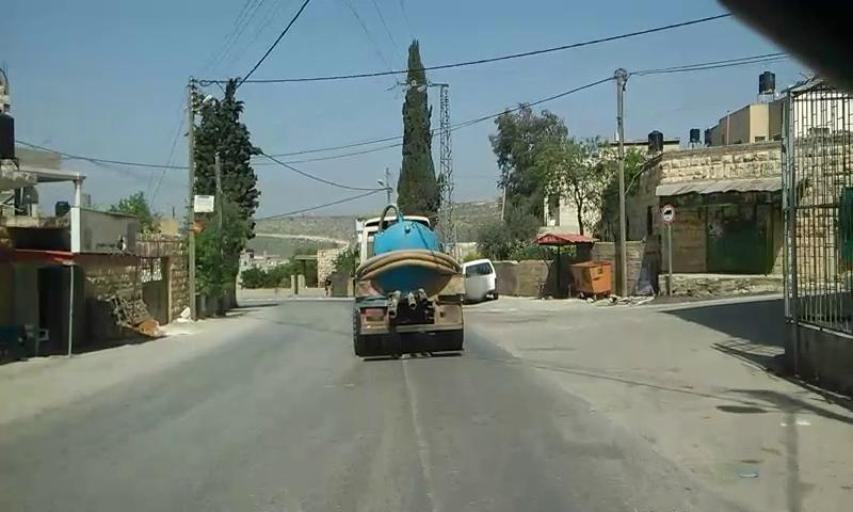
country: PS
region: West Bank
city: Az Zababidah
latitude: 32.3883
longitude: 35.3227
